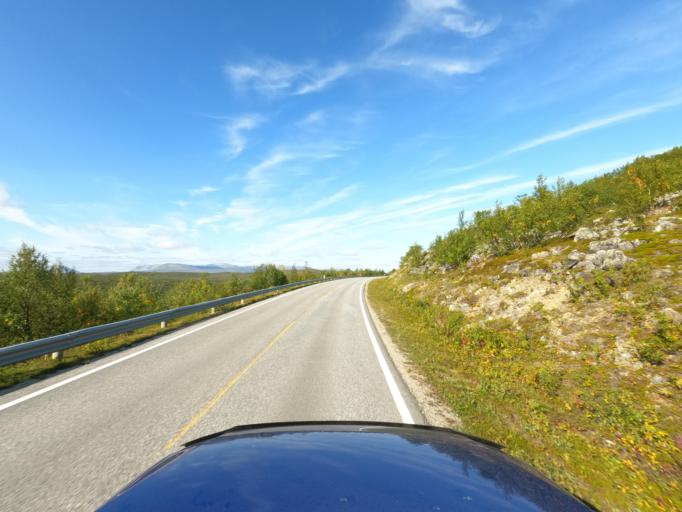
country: NO
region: Finnmark Fylke
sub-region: Porsanger
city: Lakselv
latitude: 69.7686
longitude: 25.1690
